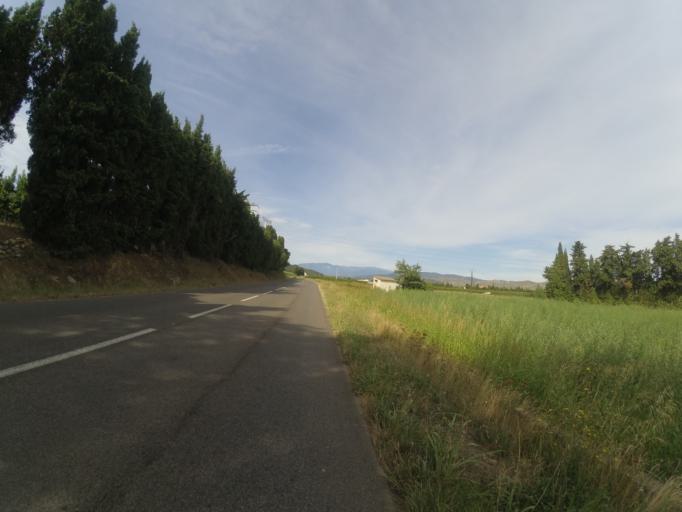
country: FR
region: Languedoc-Roussillon
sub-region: Departement des Pyrenees-Orientales
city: Ille-sur-Tet
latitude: 42.6574
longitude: 2.6401
